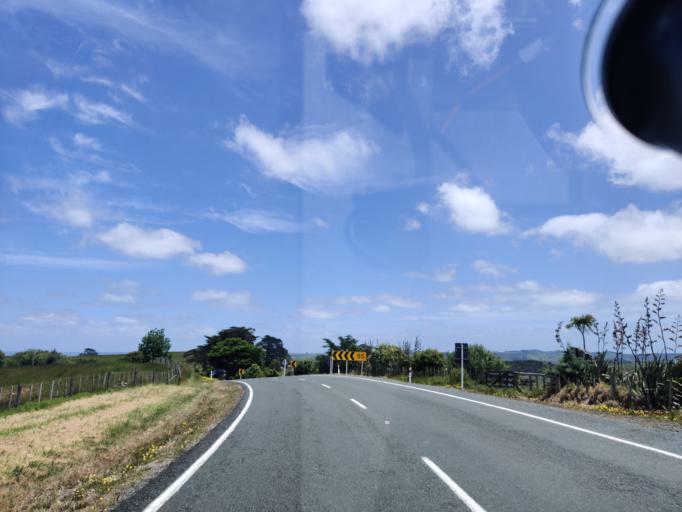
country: NZ
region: Auckland
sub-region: Auckland
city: Wellsford
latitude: -36.3663
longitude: 174.4509
